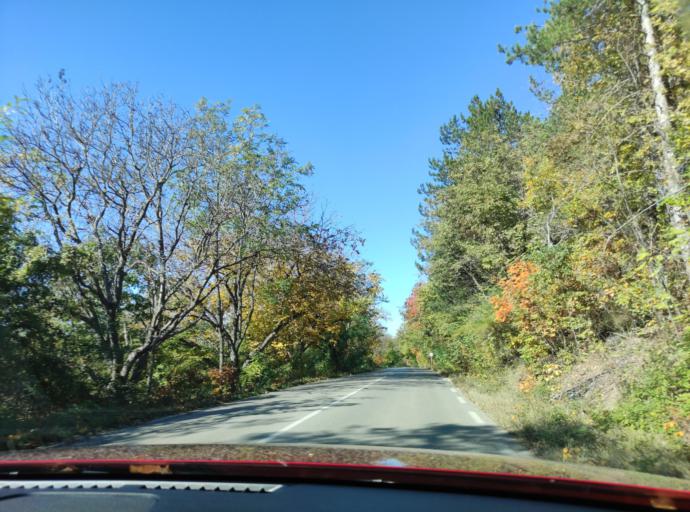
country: BG
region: Montana
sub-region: Obshtina Montana
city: Montana
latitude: 43.3988
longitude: 23.0957
